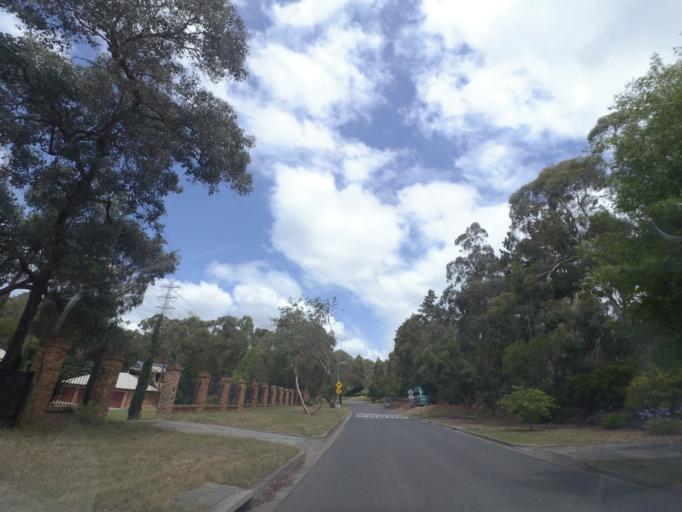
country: AU
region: Victoria
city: Mitcham
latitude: -37.8018
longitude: 145.2130
